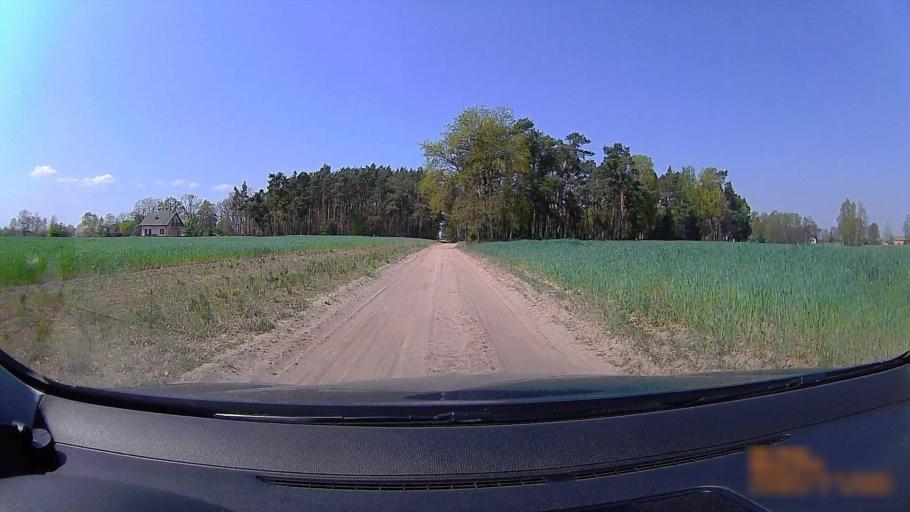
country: PL
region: Greater Poland Voivodeship
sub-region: Powiat koninski
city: Rychwal
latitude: 52.1023
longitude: 18.1757
